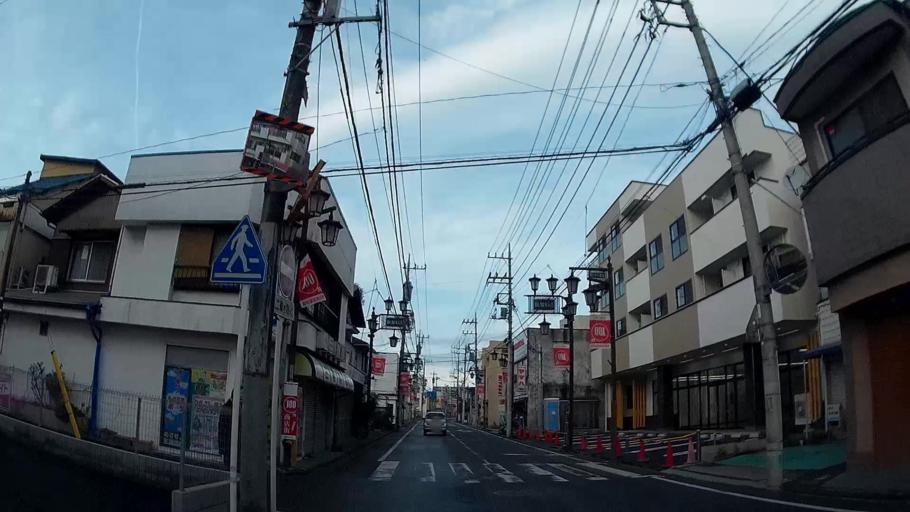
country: JP
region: Saitama
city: Hanno
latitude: 35.8518
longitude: 139.3227
